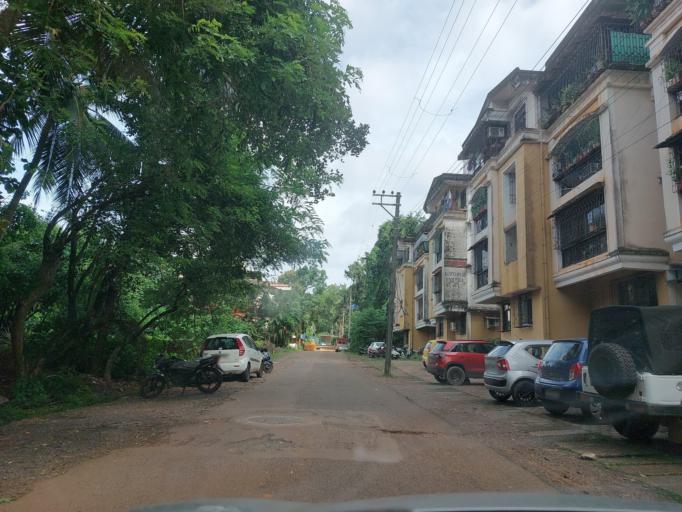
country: IN
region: Goa
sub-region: North Goa
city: Ponda
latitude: 15.3969
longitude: 74.0076
